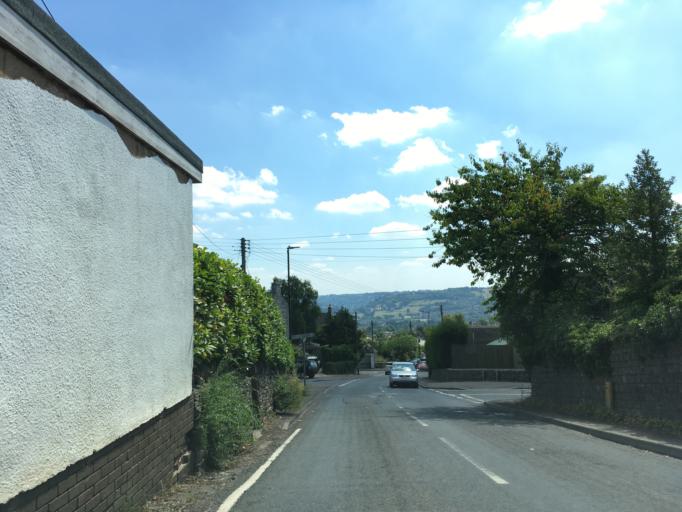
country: GB
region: England
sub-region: Gloucestershire
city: Stroud
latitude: 51.7645
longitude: -2.2345
